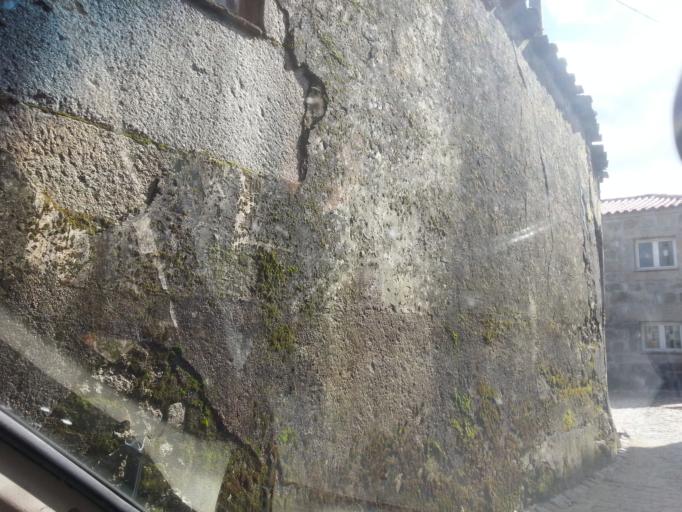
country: PT
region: Guarda
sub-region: Fornos de Algodres
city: Fornos de Algodres
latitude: 40.6459
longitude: -7.5163
